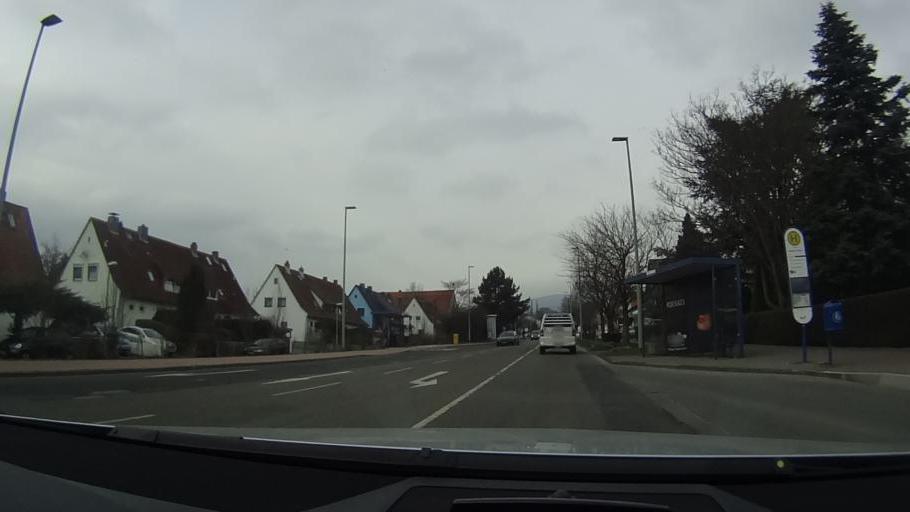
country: DE
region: Hesse
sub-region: Regierungsbezirk Darmstadt
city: Kronberg
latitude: 50.1730
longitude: 8.5252
